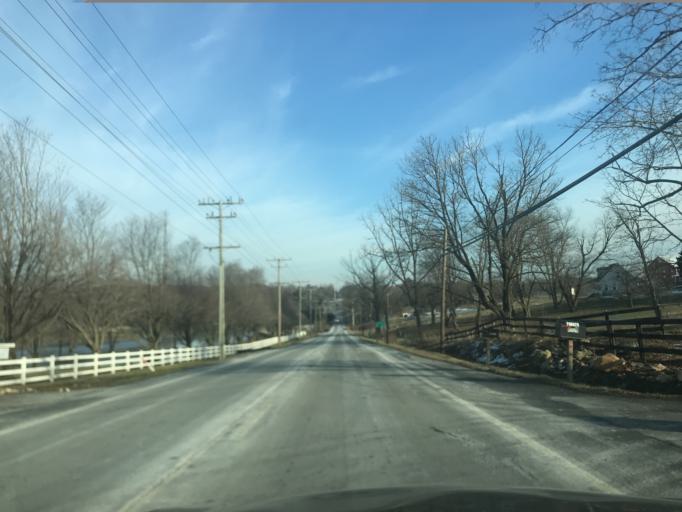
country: US
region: Maryland
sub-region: Carroll County
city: Sykesville
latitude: 39.3048
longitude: -76.9617
